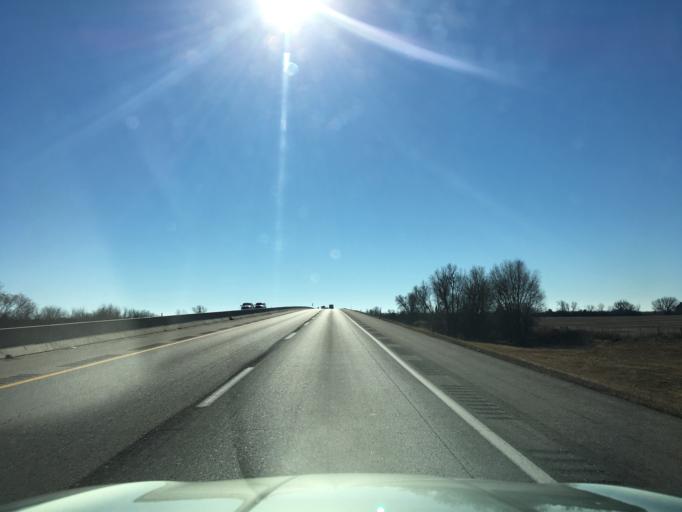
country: US
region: Kansas
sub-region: Sumner County
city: Wellington
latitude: 37.0766
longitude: -97.3386
